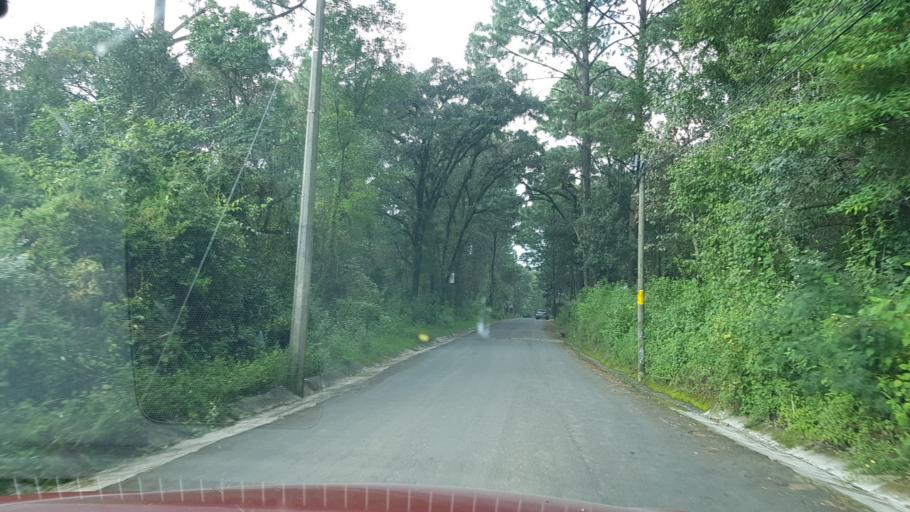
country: MX
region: Mexico
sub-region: Valle de Bravo
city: San Juan Atezcapan
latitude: 19.1511
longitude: -100.1488
